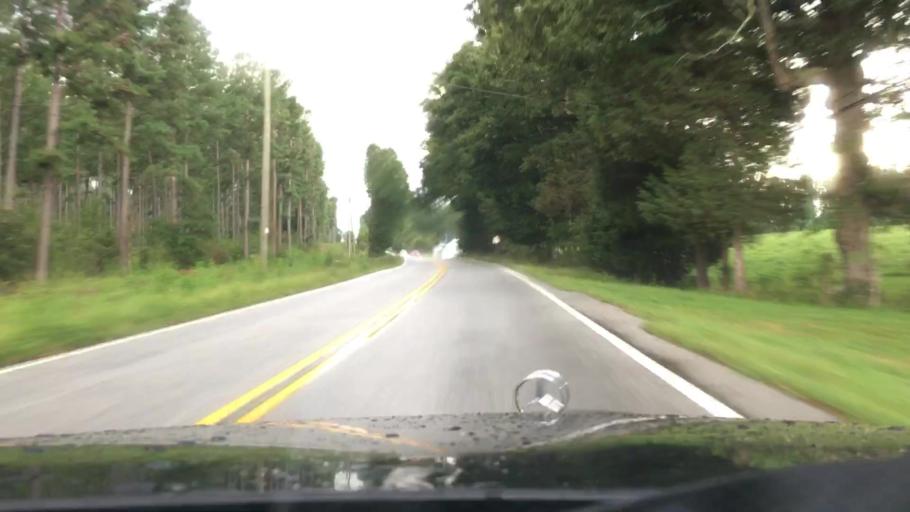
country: US
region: Virginia
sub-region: Nelson County
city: Lovingston
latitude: 37.7483
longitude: -78.9934
